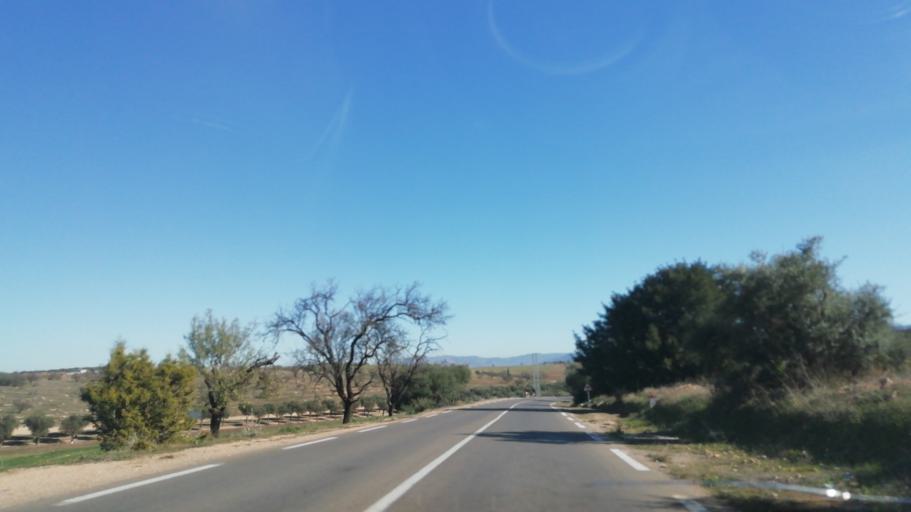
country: DZ
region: Tlemcen
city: Beni Mester
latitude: 34.8271
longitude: -1.6011
